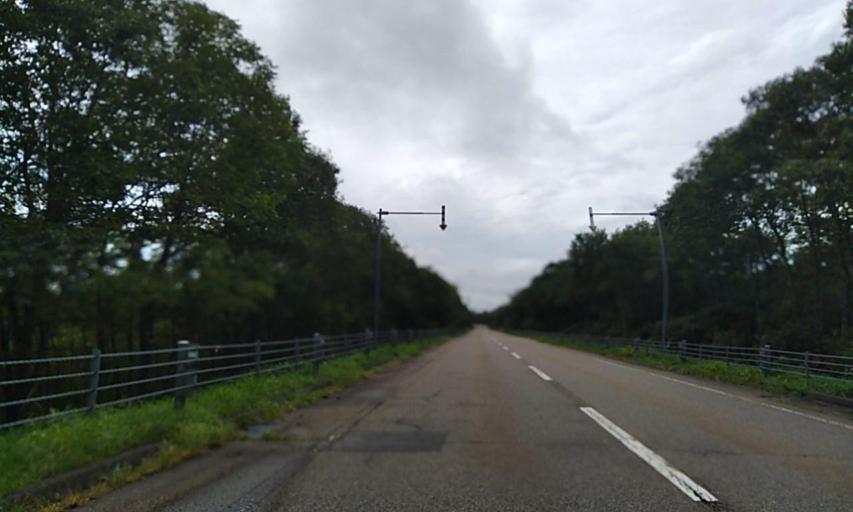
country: JP
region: Hokkaido
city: Shibetsu
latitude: 43.3564
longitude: 145.2175
